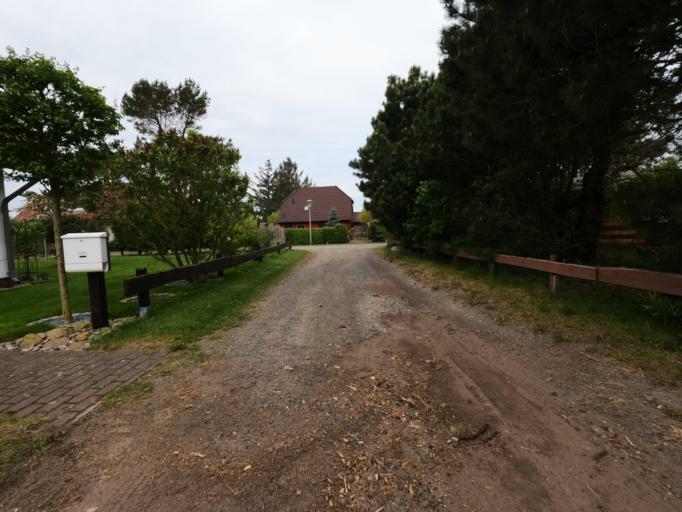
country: DE
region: Mecklenburg-Vorpommern
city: Born
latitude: 54.3637
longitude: 12.5640
